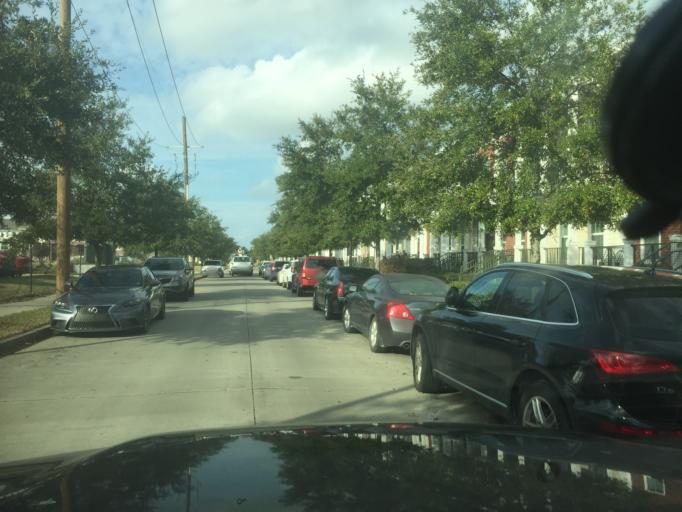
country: US
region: Louisiana
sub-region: Orleans Parish
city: New Orleans
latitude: 29.9960
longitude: -90.0771
